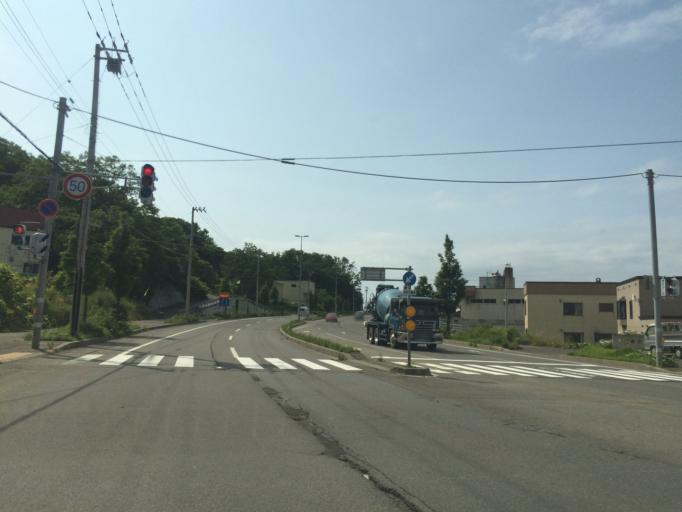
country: JP
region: Hokkaido
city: Otaru
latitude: 43.2087
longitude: 140.9227
